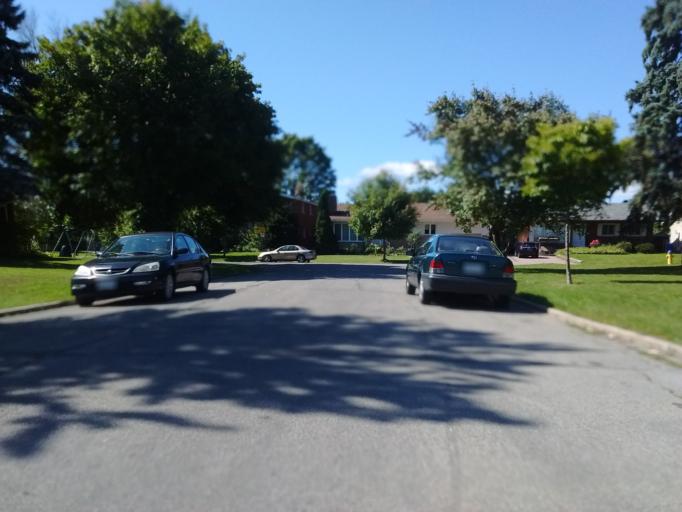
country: CA
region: Ontario
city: Ottawa
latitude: 45.4321
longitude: -75.6378
